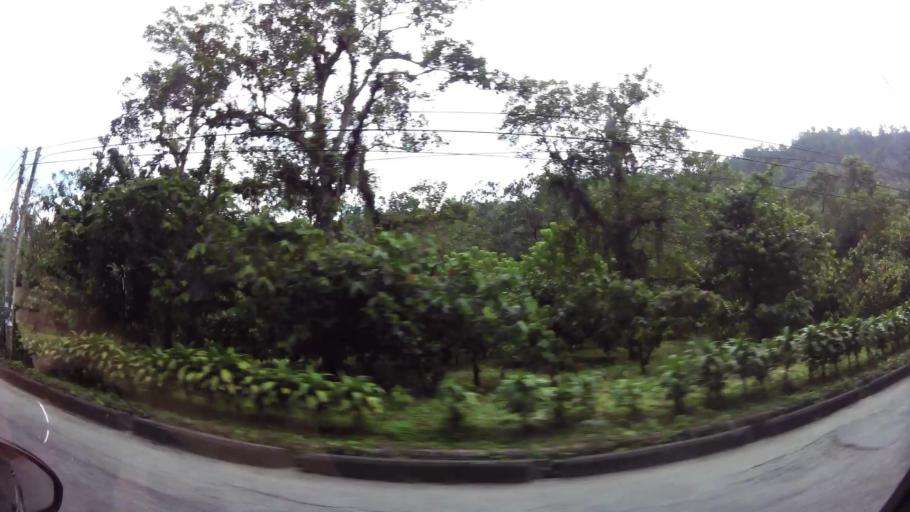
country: TT
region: San Juan/Laventille
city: Laventille
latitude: 10.6921
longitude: -61.4579
